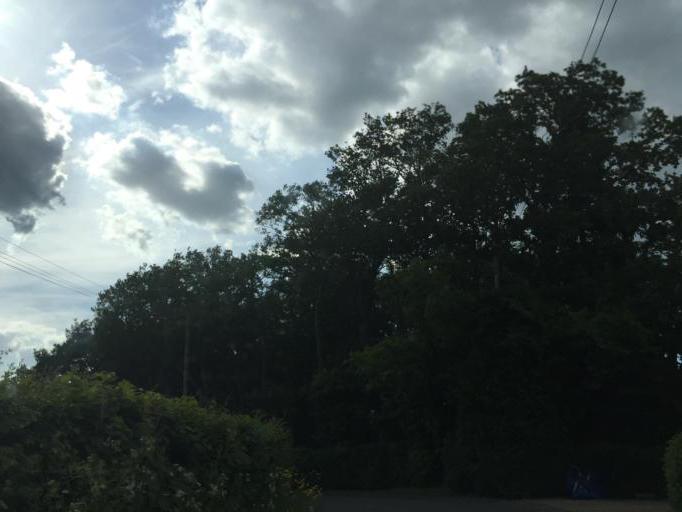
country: GB
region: England
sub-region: East Sussex
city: Wadhurst
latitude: 51.0337
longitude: 0.2838
